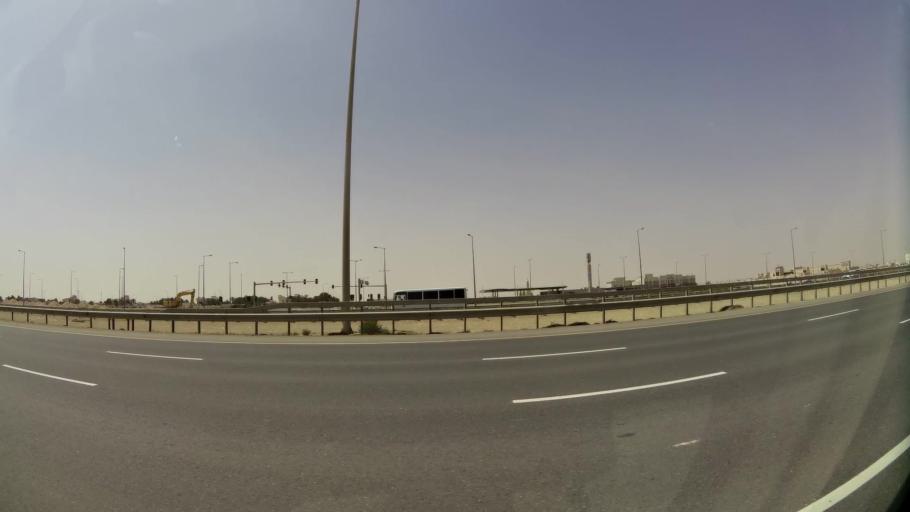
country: QA
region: Baladiyat Umm Salal
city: Umm Salal Muhammad
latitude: 25.4338
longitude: 51.4134
